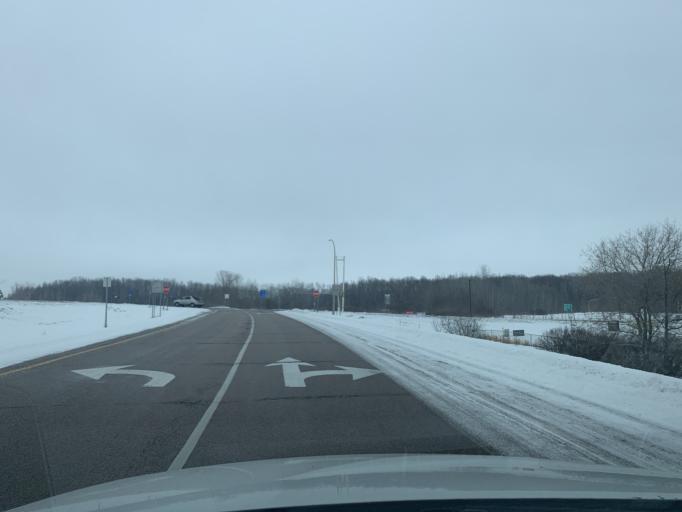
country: US
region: Minnesota
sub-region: Chisago County
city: Rush City
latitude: 45.6834
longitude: -92.9887
